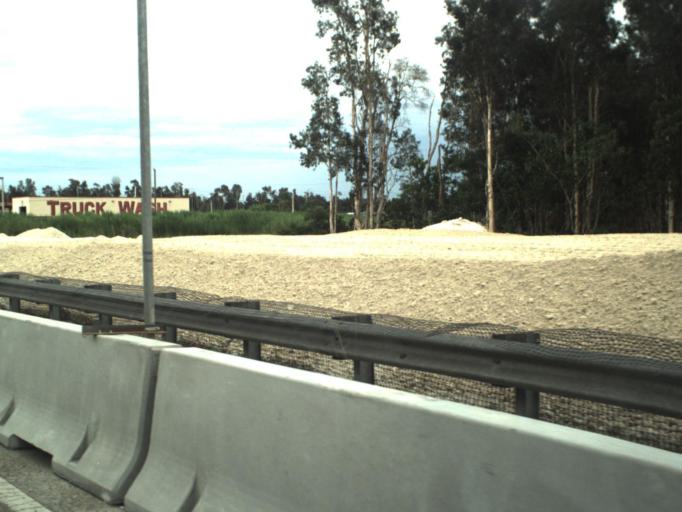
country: US
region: Florida
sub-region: Miami-Dade County
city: Kendall West
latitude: 25.7583
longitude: -80.4813
